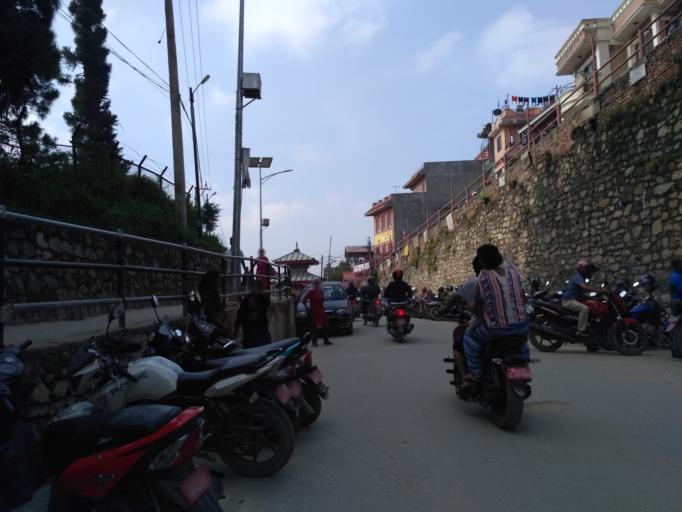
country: NP
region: Central Region
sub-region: Bagmati Zone
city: Kathmandu
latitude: 27.7120
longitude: 85.3473
